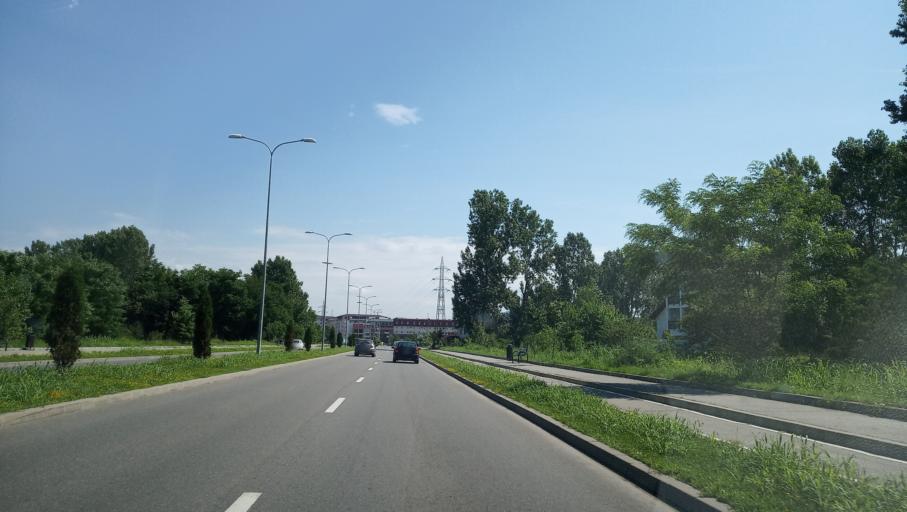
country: RO
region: Valcea
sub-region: Municipiul Ramnicu Valcea
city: Ramnicu Valcea
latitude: 45.0787
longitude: 24.3636
